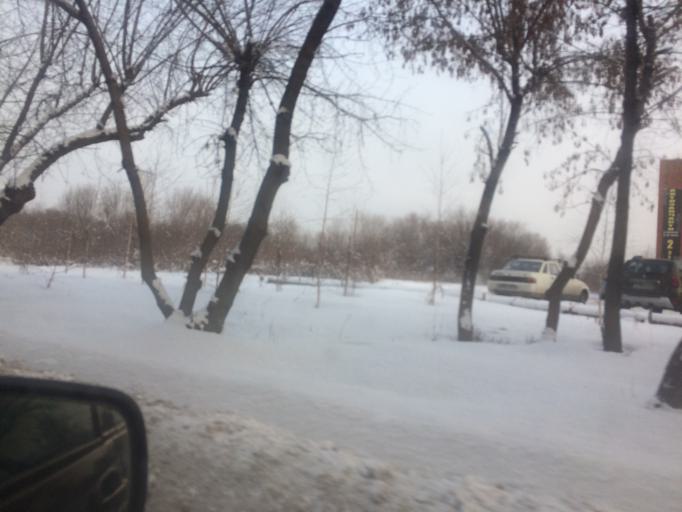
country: RU
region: Chelyabinsk
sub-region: Gorod Magnitogorsk
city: Magnitogorsk
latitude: 53.4661
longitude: 59.0726
